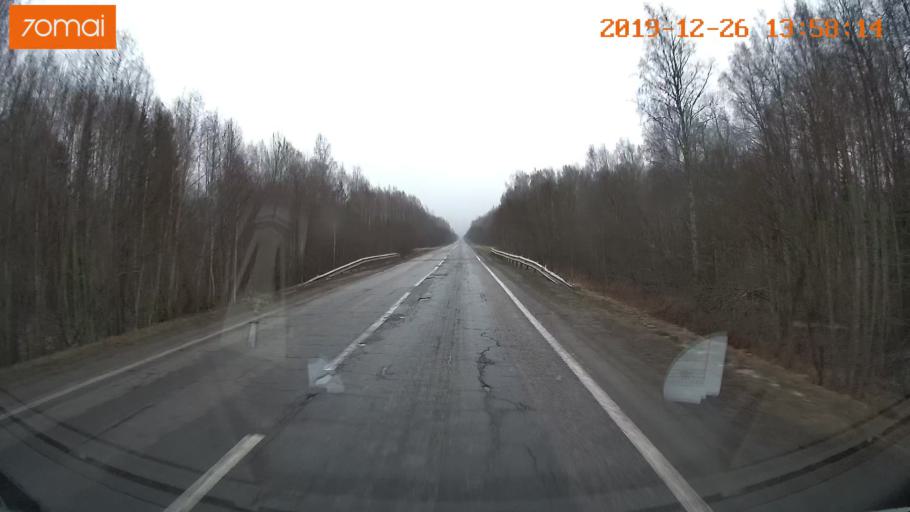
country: RU
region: Jaroslavl
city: Poshekhon'ye
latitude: 58.5758
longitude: 38.6963
